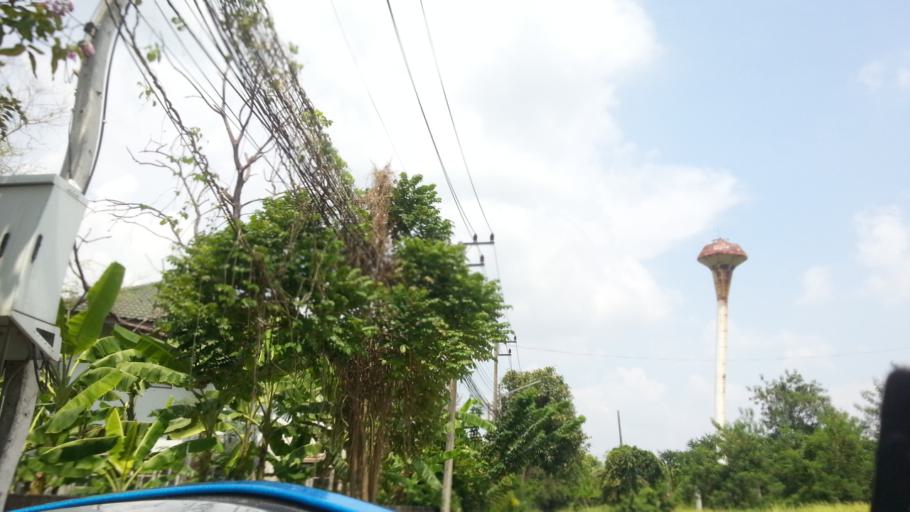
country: TH
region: Pathum Thani
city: Ban Rangsit
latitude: 14.0444
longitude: 100.8303
